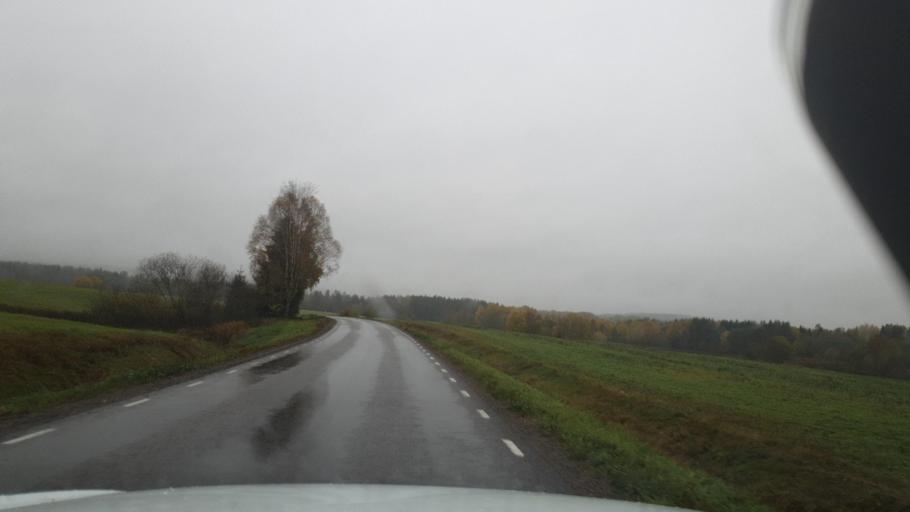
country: SE
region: Vaermland
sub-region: Eda Kommun
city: Charlottenberg
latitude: 59.7835
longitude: 12.1608
